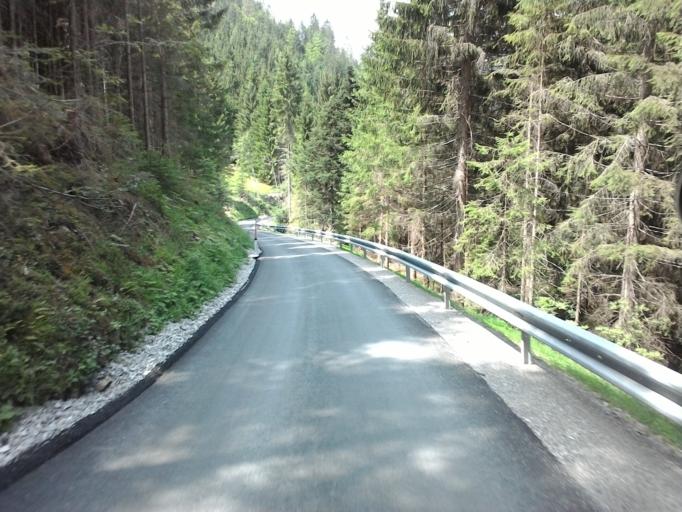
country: AT
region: Tyrol
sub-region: Politischer Bezirk Lienz
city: Untertilliach
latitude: 46.6993
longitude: 12.7722
